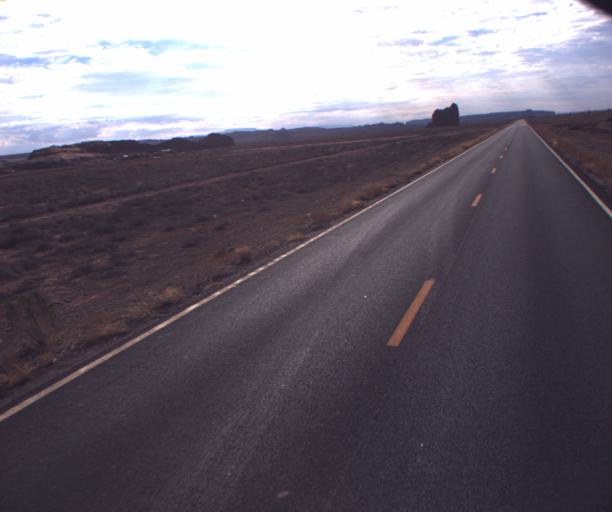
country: US
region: Arizona
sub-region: Apache County
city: Many Farms
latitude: 36.7547
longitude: -109.6461
